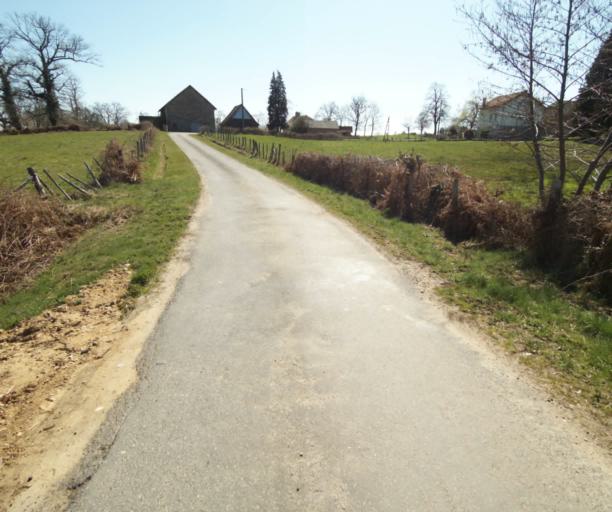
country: FR
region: Limousin
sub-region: Departement de la Correze
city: Saint-Clement
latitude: 45.3078
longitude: 1.6990
